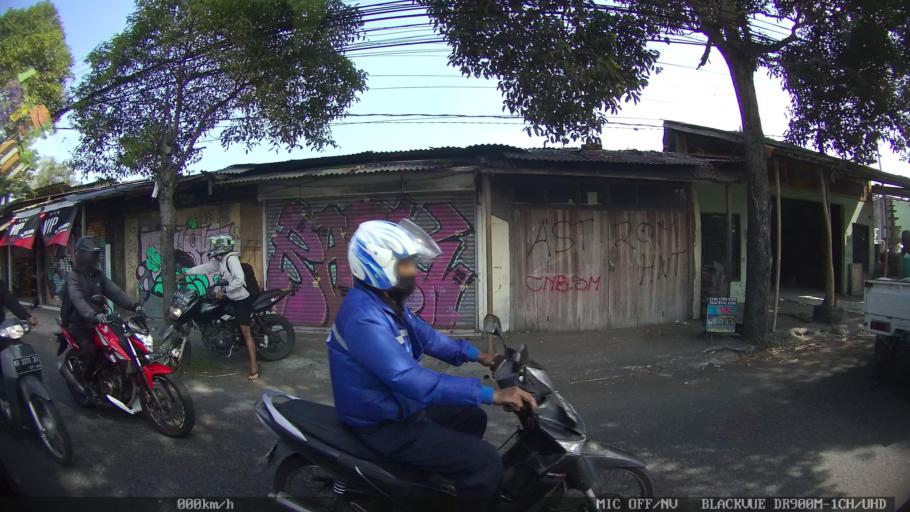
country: ID
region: Daerah Istimewa Yogyakarta
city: Kasihan
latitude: -7.8467
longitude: 110.3435
